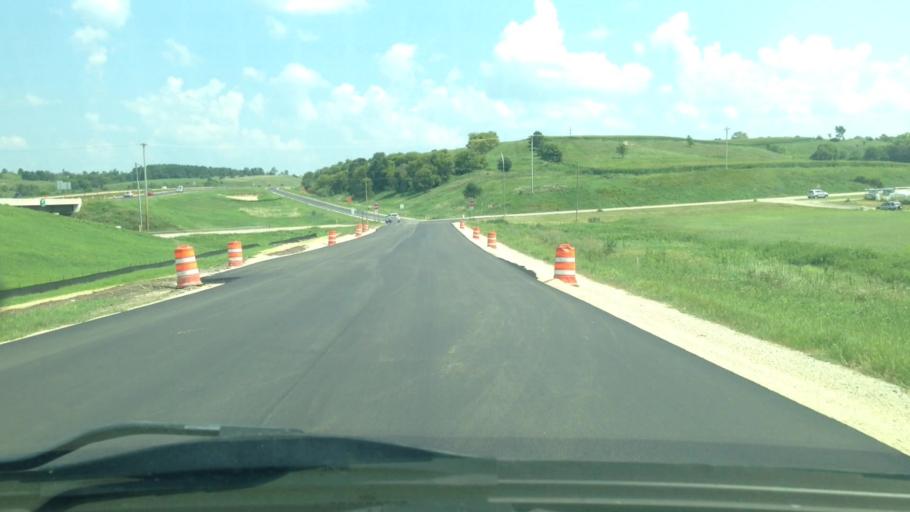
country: US
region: Minnesota
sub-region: Olmsted County
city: Rochester
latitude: 43.9737
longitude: -92.4412
